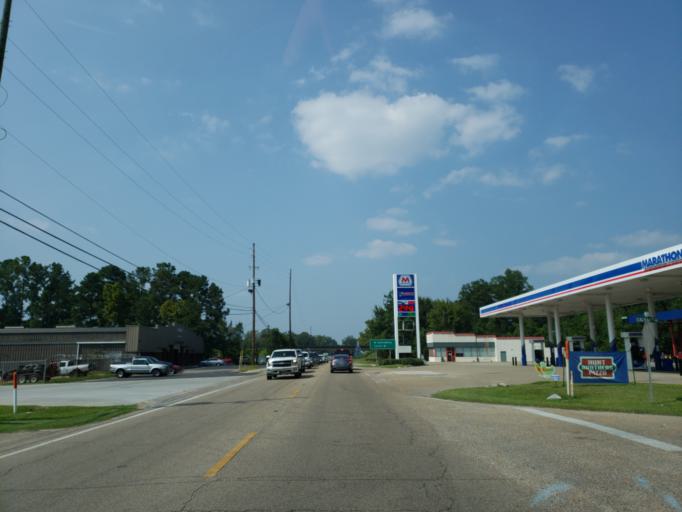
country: US
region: Mississippi
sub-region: Jones County
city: Ellisville
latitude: 31.6314
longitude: -89.1809
